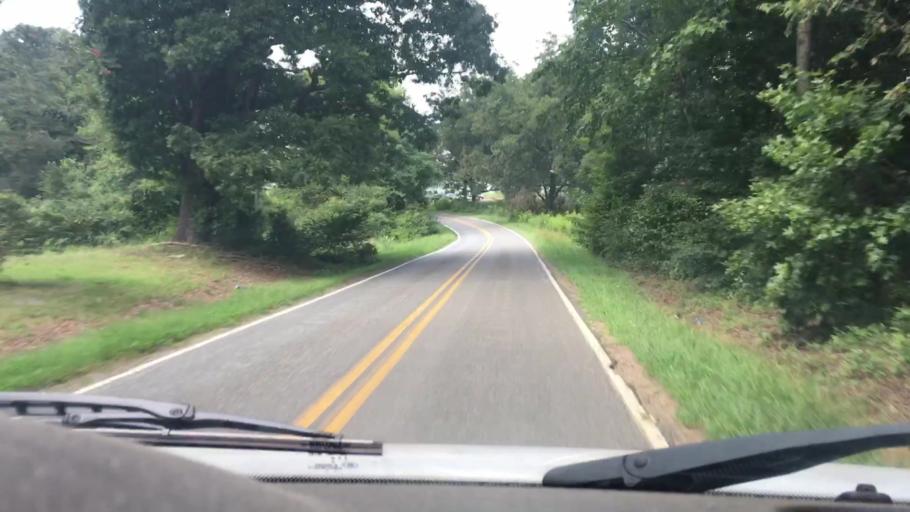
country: US
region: North Carolina
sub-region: Iredell County
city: Troutman
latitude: 35.6684
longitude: -80.8324
